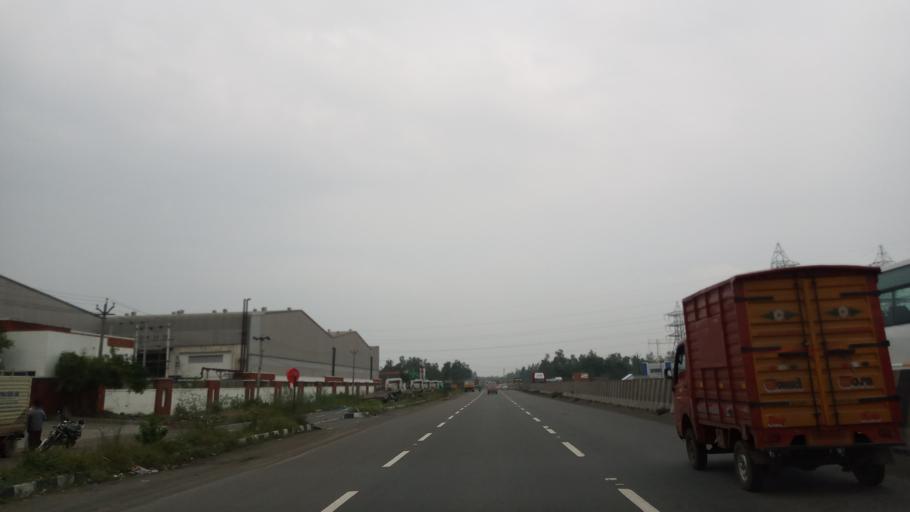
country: IN
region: Tamil Nadu
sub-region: Kancheepuram
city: Madambakkam
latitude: 12.8544
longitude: 79.9487
